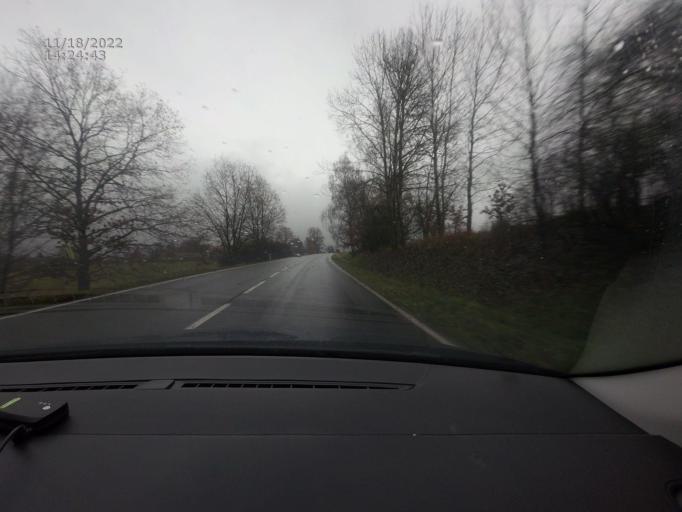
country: CZ
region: Jihocesky
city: Cimelice
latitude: 49.4380
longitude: 14.1377
